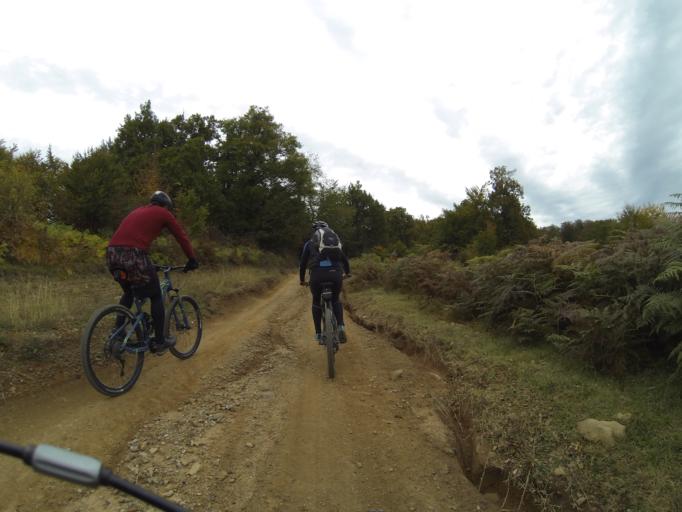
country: RO
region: Gorj
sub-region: Comuna Tismana
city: Sohodol
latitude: 45.0695
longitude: 22.8621
